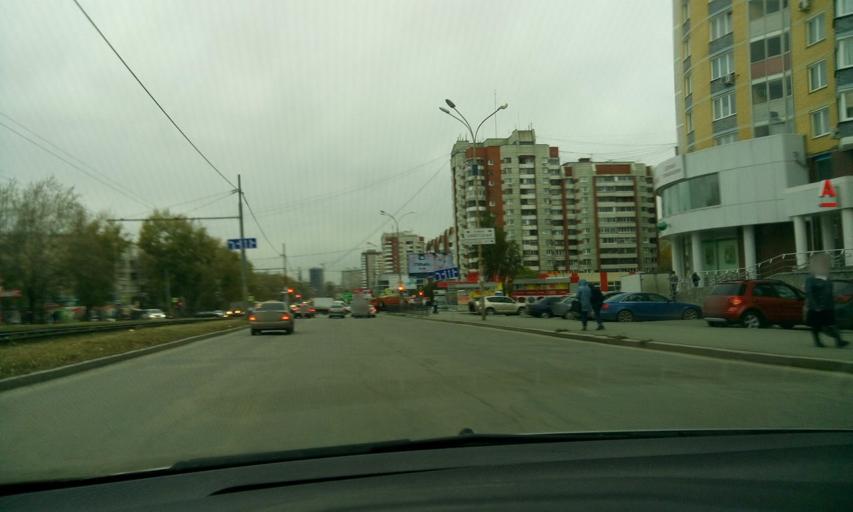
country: RU
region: Sverdlovsk
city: Yekaterinburg
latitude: 56.8535
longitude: 60.6377
